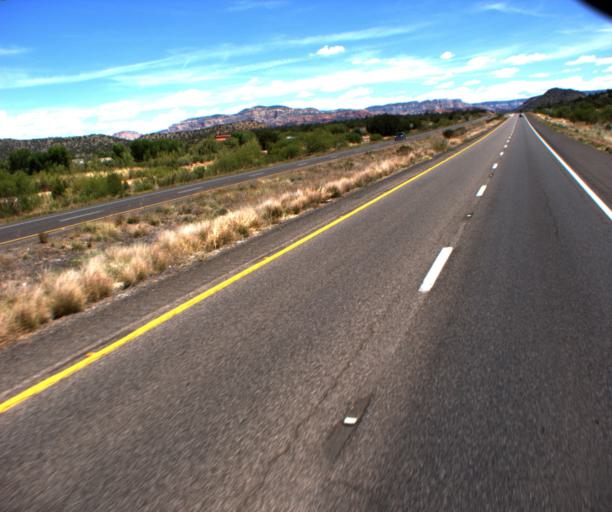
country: US
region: Arizona
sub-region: Yavapai County
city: West Sedona
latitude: 34.8277
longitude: -111.8951
